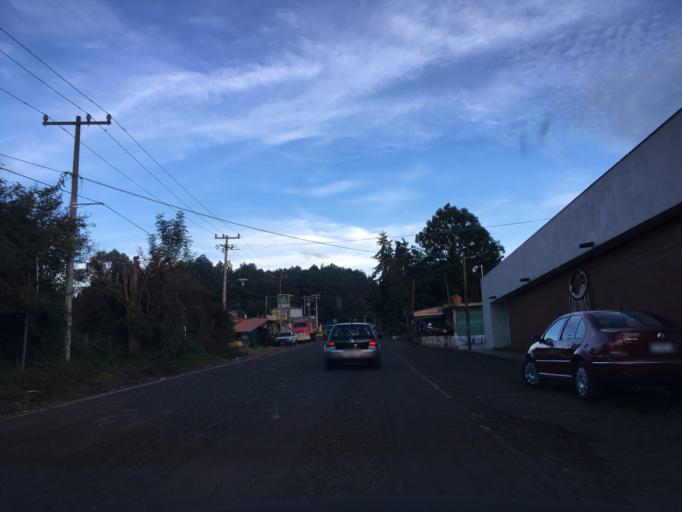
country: MX
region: Michoacan
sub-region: Salvador Escalante
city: Santa Clara del Cobre
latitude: 19.4012
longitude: -101.6520
